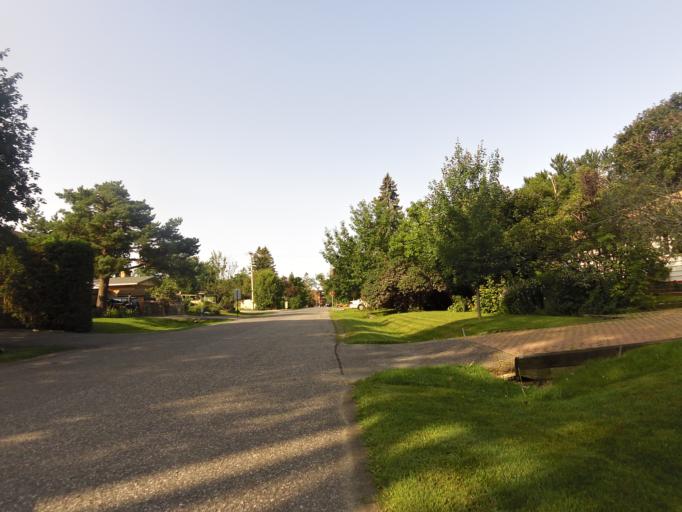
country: CA
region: Ontario
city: Ottawa
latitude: 45.3563
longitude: -75.7477
